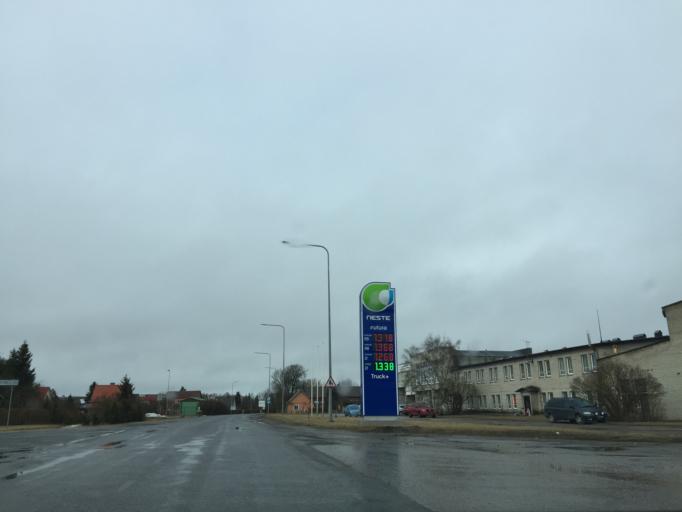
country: EE
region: Laeaene
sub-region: Haapsalu linn
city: Haapsalu
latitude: 58.9254
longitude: 23.5457
